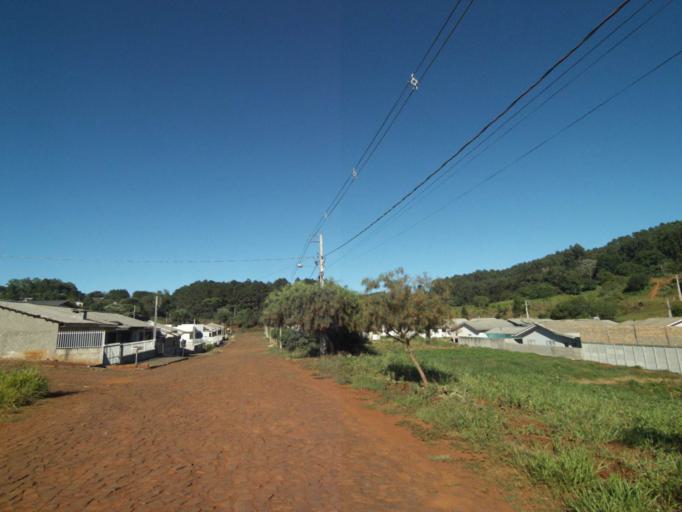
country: BR
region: Santa Catarina
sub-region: Sao Lourenco Do Oeste
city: Sao Lourenco dOeste
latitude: -26.2661
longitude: -52.7858
